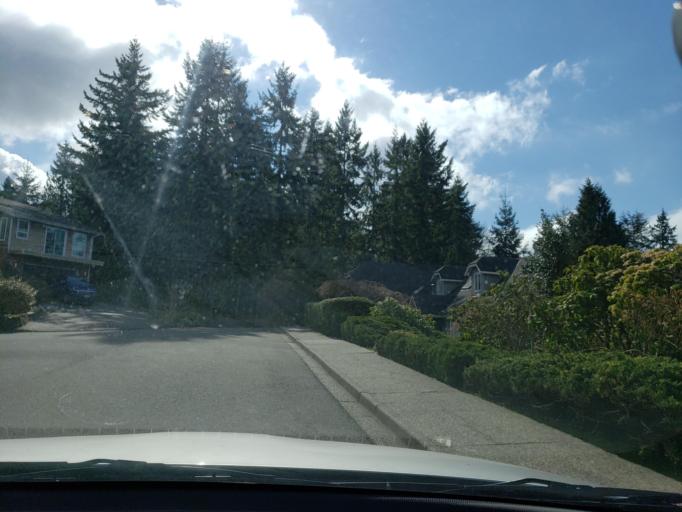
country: US
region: Washington
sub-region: Snohomish County
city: Edmonds
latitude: 47.8112
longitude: -122.3569
